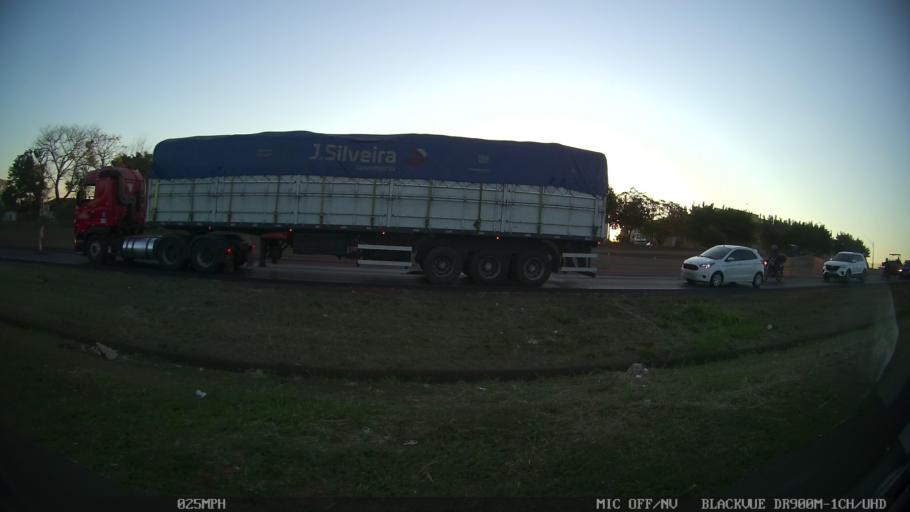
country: BR
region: Sao Paulo
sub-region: Sao Jose Do Rio Preto
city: Sao Jose do Rio Preto
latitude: -20.8051
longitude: -49.3559
